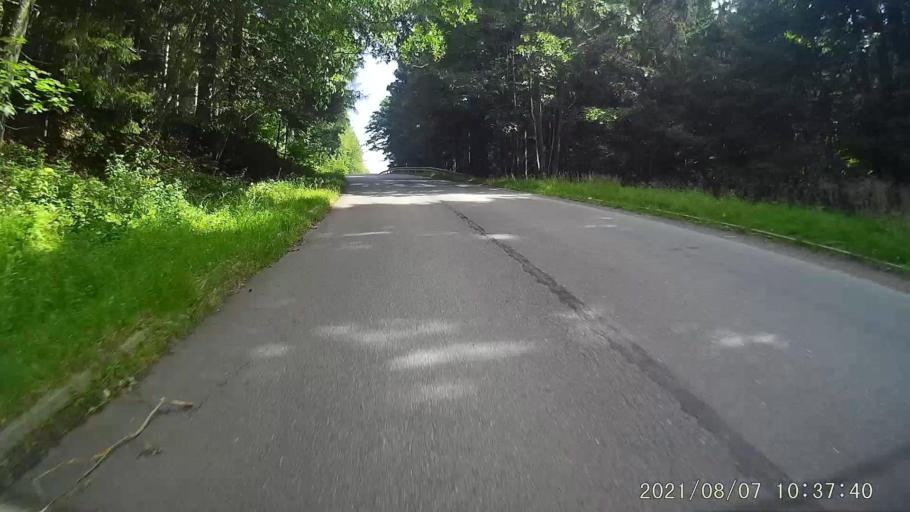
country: PL
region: Lower Silesian Voivodeship
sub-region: Powiat klodzki
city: Duszniki-Zdroj
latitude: 50.3542
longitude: 16.3718
